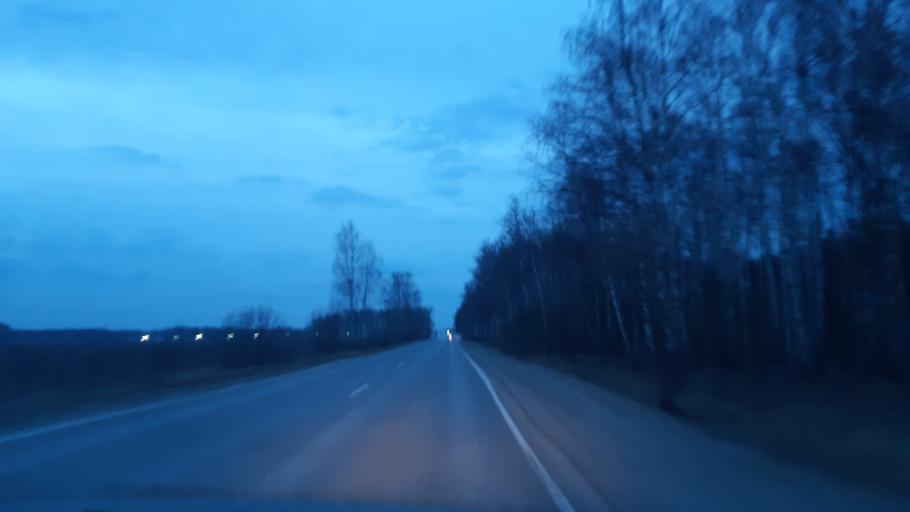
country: RU
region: Vladimir
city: Luknovo
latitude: 56.2304
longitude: 42.0346
